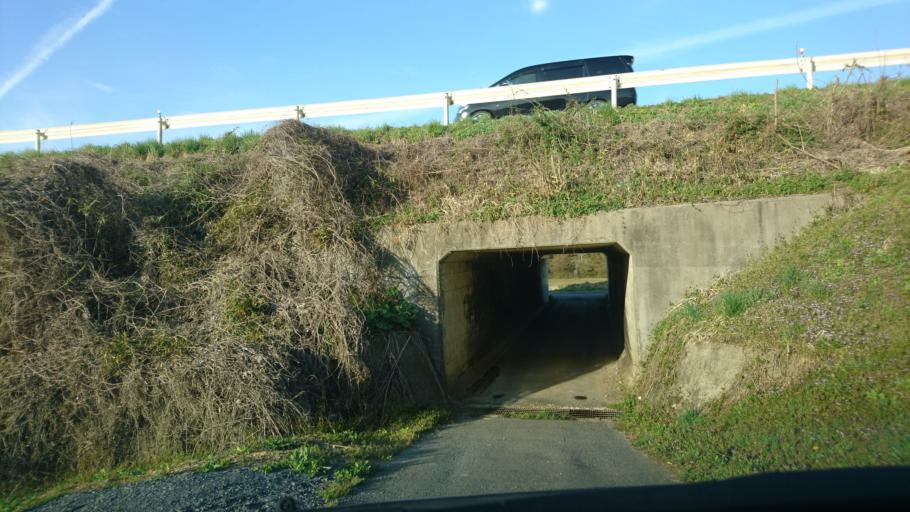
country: JP
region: Iwate
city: Ichinoseki
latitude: 38.9024
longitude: 141.2230
